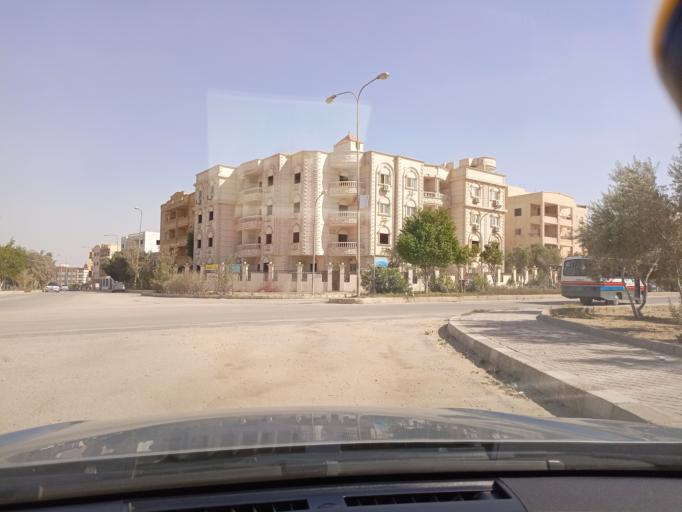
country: EG
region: Muhafazat al Qalyubiyah
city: Al Khankah
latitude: 30.2281
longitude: 31.4452
